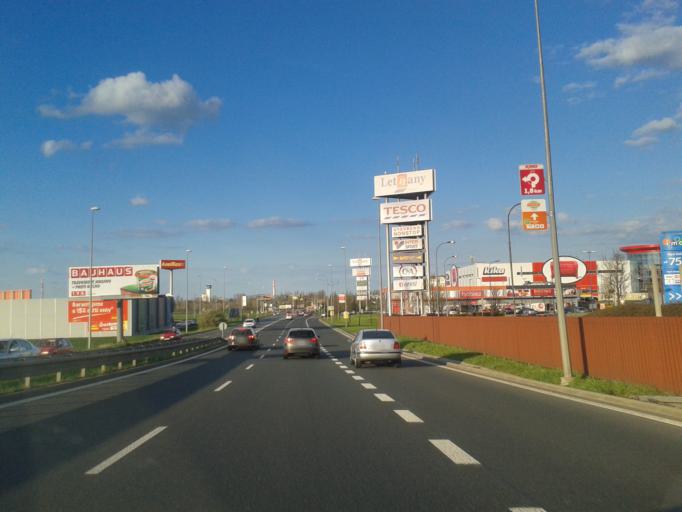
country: CZ
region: Praha
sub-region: Praha 9
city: Strizkov
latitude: 50.1376
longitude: 14.4972
